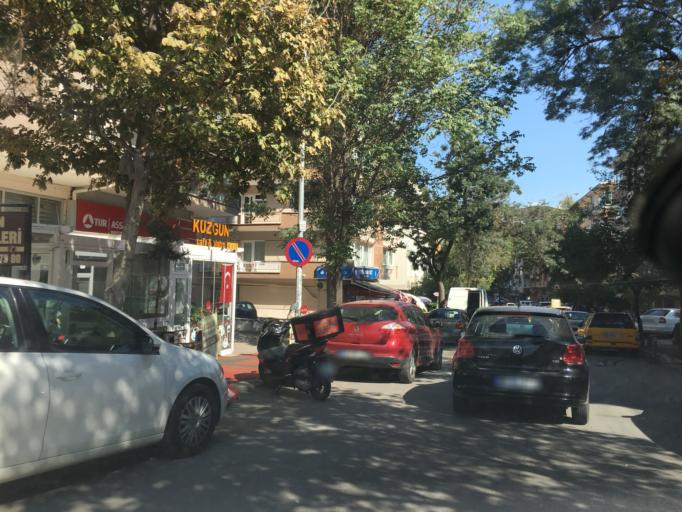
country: TR
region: Ankara
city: Ankara
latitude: 39.8978
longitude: 32.8505
